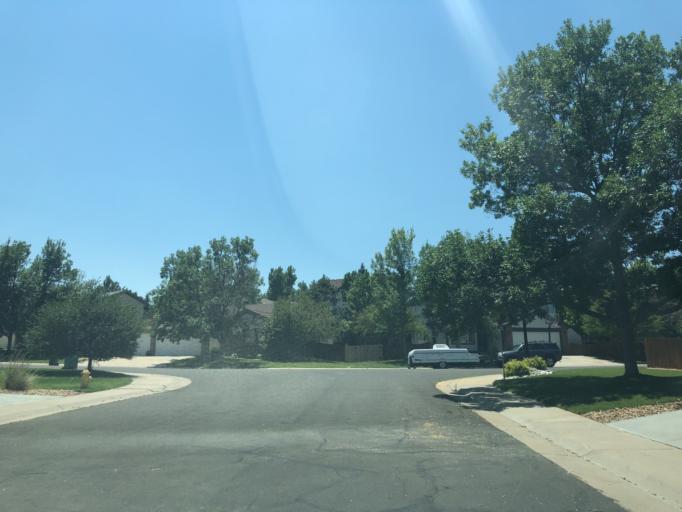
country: US
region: Colorado
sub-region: Arapahoe County
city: Dove Valley
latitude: 39.6304
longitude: -104.7647
